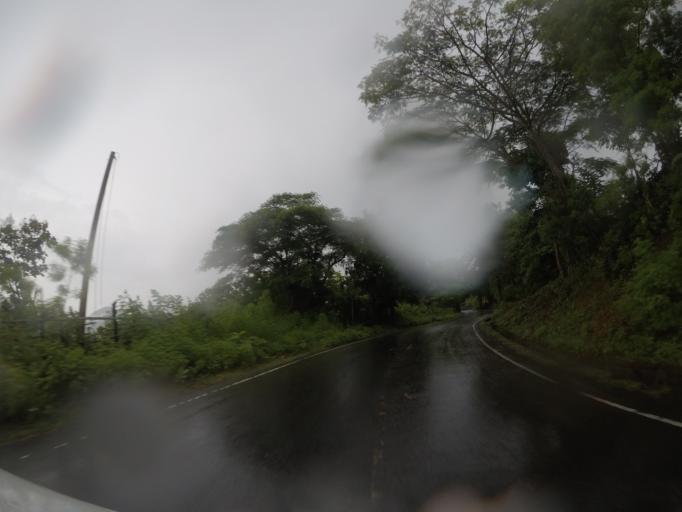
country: TL
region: Bobonaro
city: Maliana
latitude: -8.9538
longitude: 125.0689
